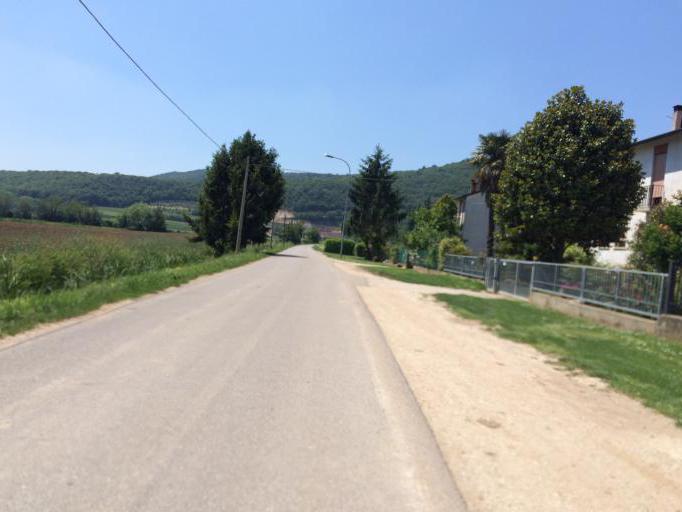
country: IT
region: Veneto
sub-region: Provincia di Vicenza
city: Villaga
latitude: 45.3893
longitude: 11.5212
